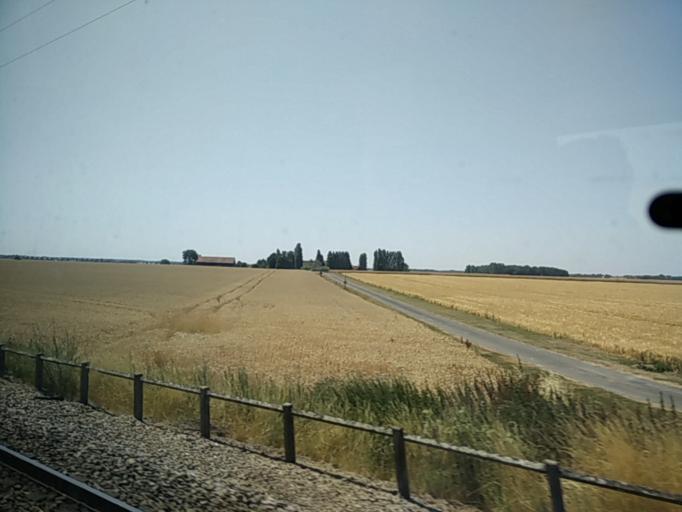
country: FR
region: Ile-de-France
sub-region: Departement de Seine-et-Marne
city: Bailly-Carrois
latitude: 48.5751
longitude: 2.9938
